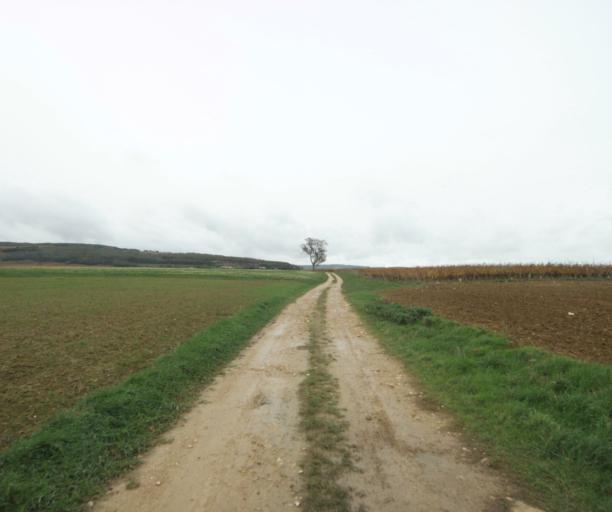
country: FR
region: Rhone-Alpes
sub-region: Departement de l'Ain
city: Pont-de-Vaux
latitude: 46.4680
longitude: 4.8657
